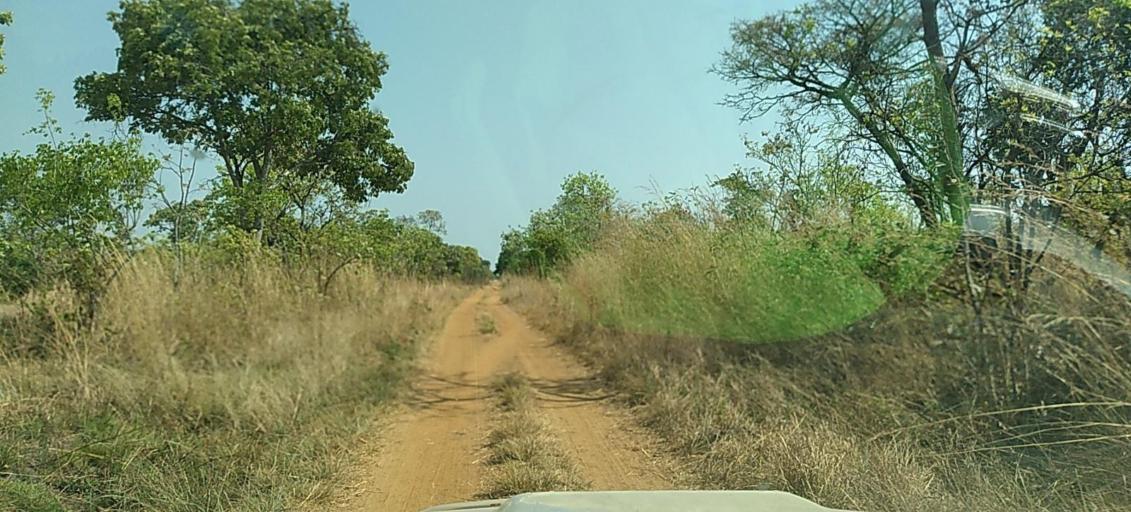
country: ZM
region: North-Western
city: Kalengwa
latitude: -13.2467
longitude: 24.7596
